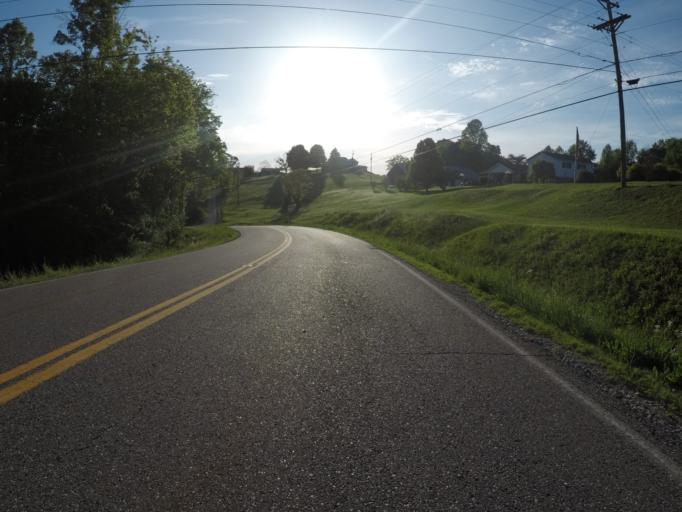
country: US
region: West Virginia
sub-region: Cabell County
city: Huntington
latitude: 38.5538
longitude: -82.4270
